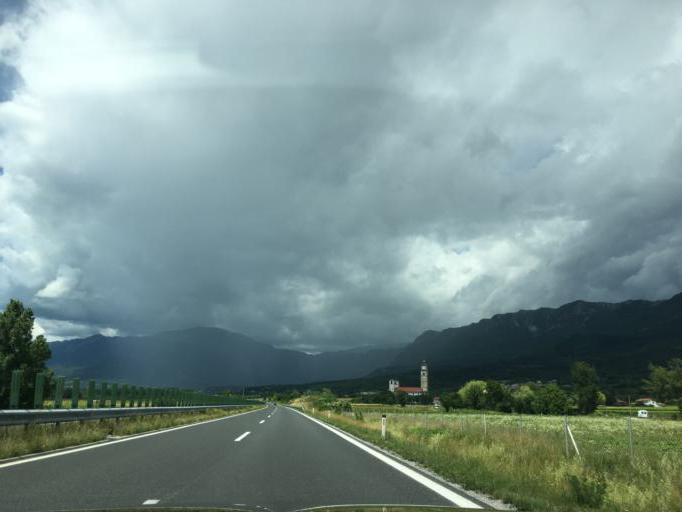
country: SI
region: Vipava
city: Vipava
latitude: 45.8588
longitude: 13.9407
